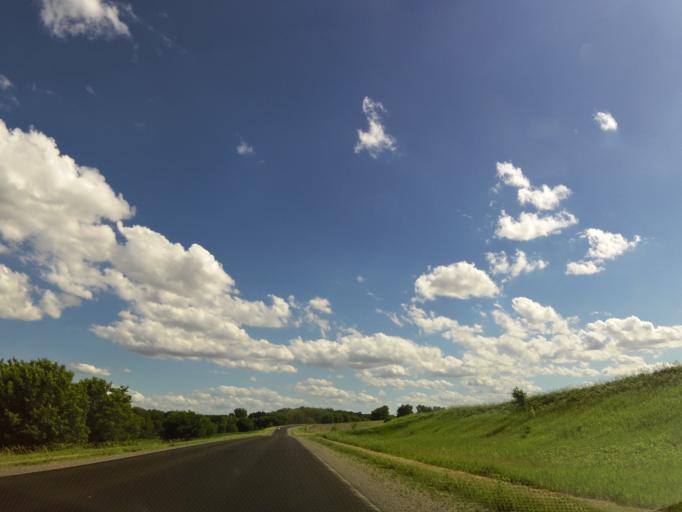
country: US
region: Minnesota
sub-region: Meeker County
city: Dassel
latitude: 45.1252
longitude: -94.2967
